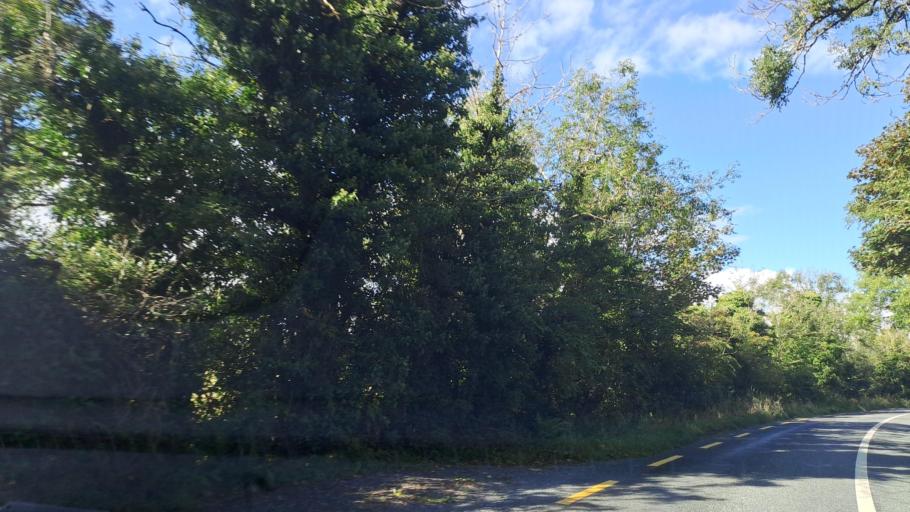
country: IE
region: Ulster
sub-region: An Cabhan
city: Kingscourt
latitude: 53.9779
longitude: -6.8783
